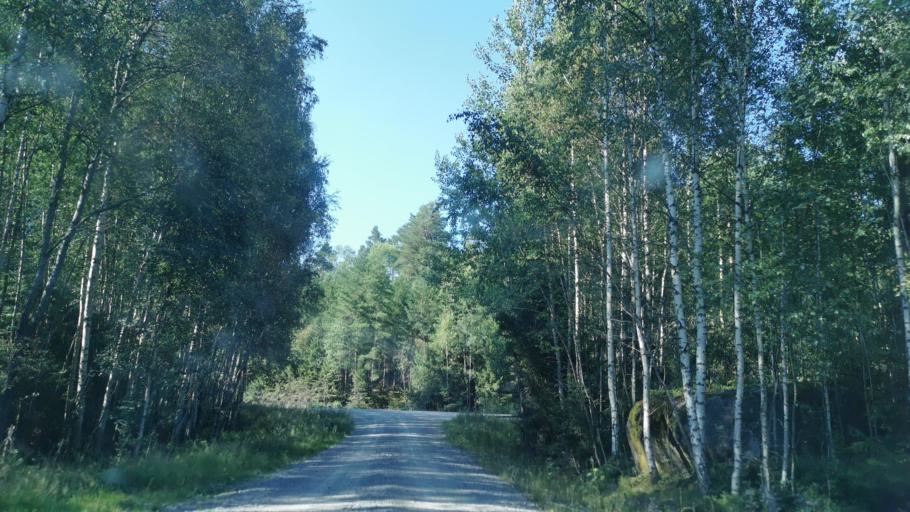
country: SE
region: OEstergoetland
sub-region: Norrkopings Kommun
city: Jursla
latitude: 58.7102
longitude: 16.1854
